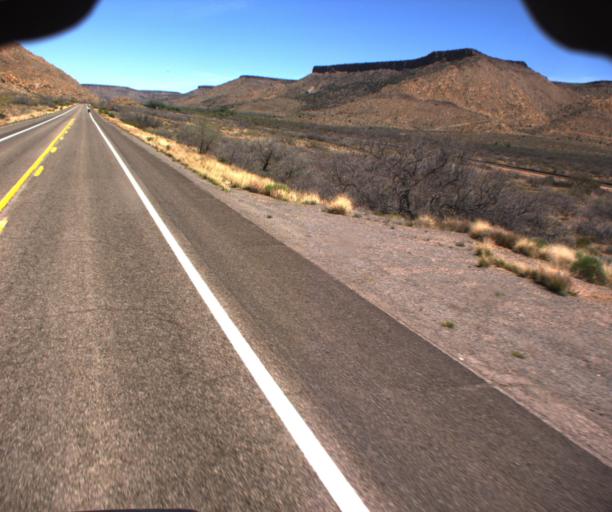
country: US
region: Arizona
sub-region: Mohave County
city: Peach Springs
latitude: 35.3737
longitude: -113.6683
